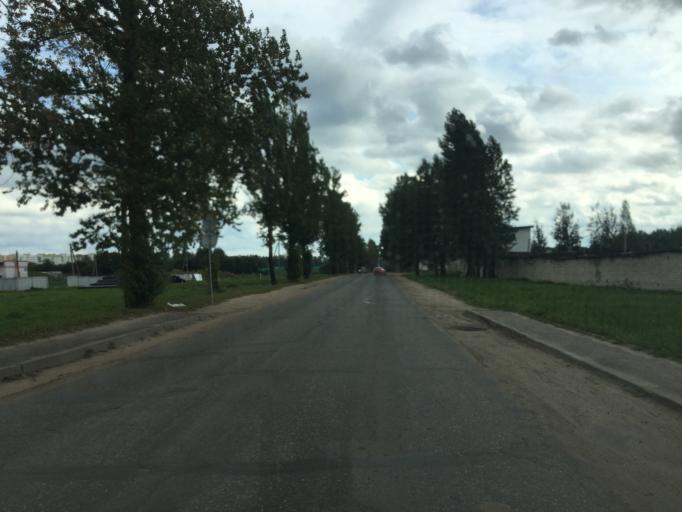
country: BY
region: Vitebsk
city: Vitebsk
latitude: 55.1654
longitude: 30.2554
